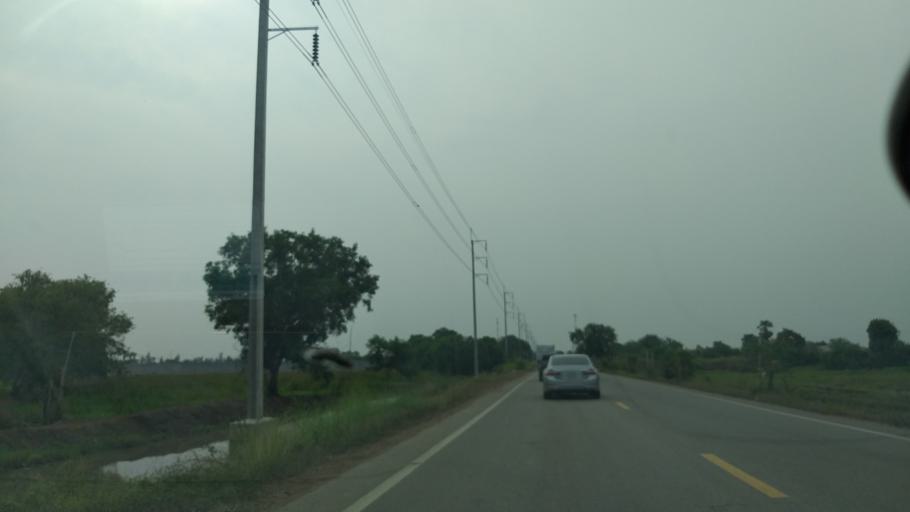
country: TH
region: Chachoengsao
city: Plaeng Yao
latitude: 13.5946
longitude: 101.1929
